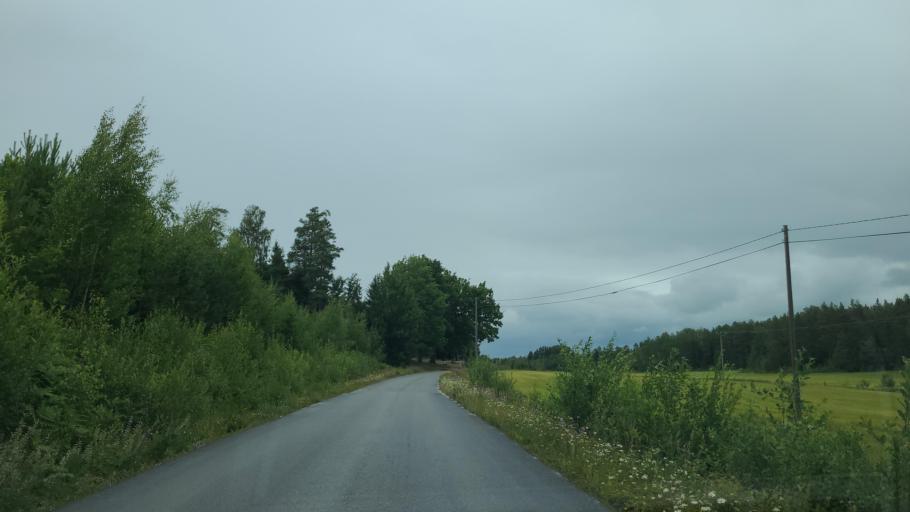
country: FI
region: Varsinais-Suomi
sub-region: Aboland-Turunmaa
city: Dragsfjaerd
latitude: 60.0888
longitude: 22.4346
